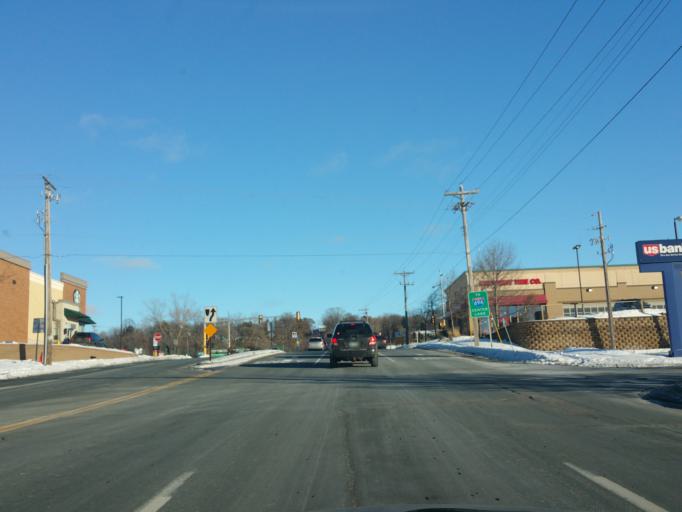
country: US
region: Minnesota
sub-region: Anoka County
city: Fridley
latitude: 45.0644
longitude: -93.2494
